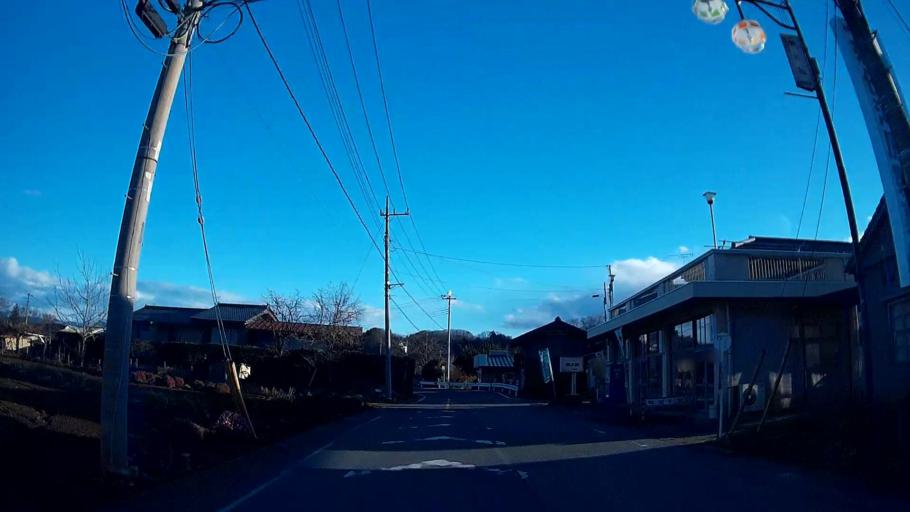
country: JP
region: Saitama
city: Chichibu
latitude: 36.0422
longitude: 139.0160
